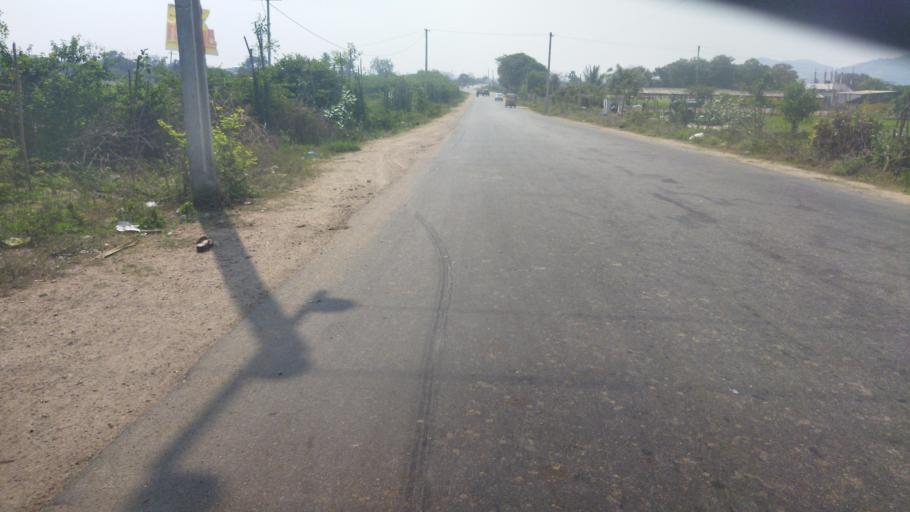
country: IN
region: Telangana
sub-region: Nalgonda
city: Nalgonda
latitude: 17.0867
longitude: 79.2847
